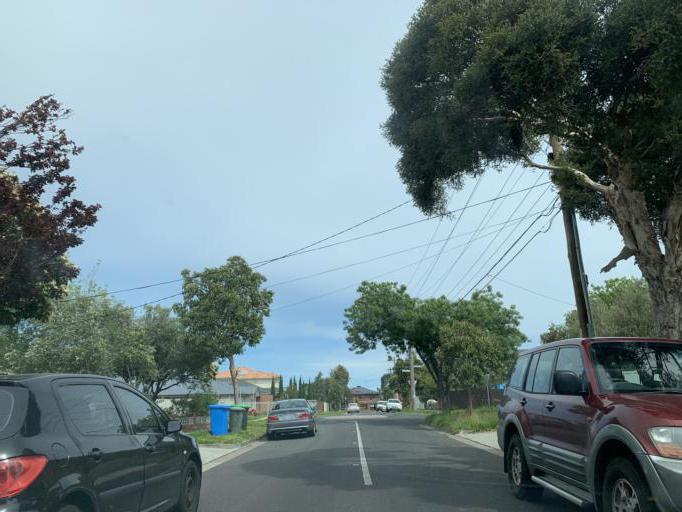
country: AU
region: Victoria
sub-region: Bayside
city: Hampton East
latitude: -37.9369
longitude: 145.0278
